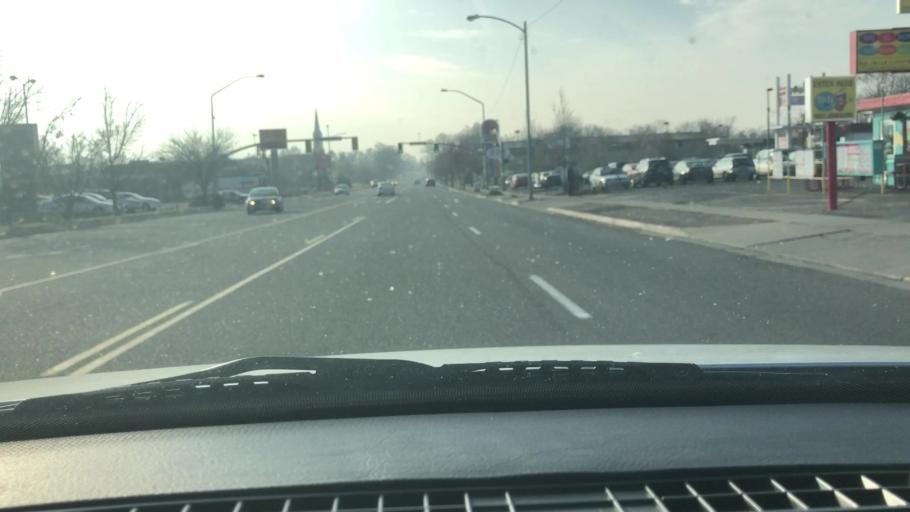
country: US
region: Utah
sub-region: Utah County
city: Provo
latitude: 40.2408
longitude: -111.6432
